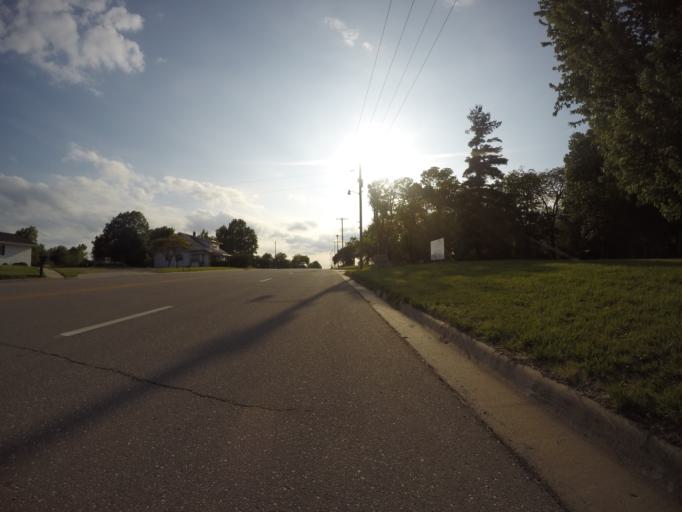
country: US
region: Kansas
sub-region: Pottawatomie County
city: Westmoreland
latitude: 39.4285
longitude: -96.6146
